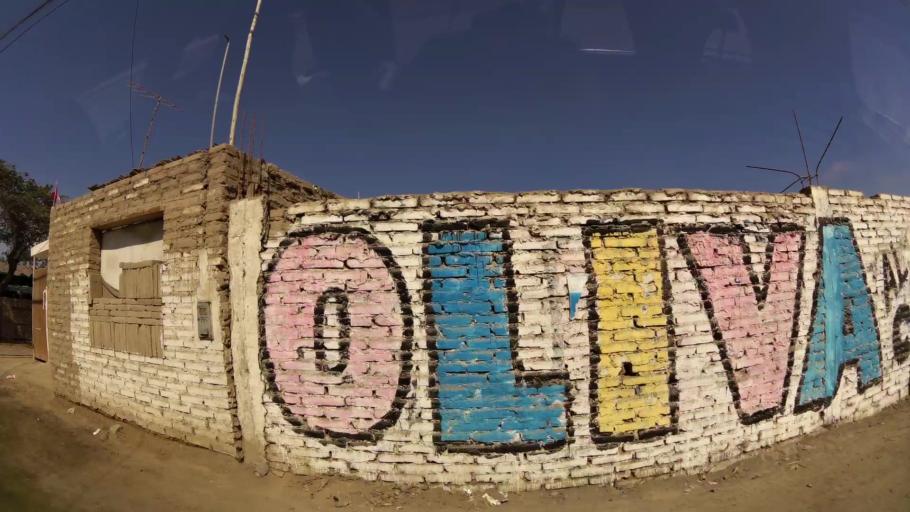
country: PE
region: Ica
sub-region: Provincia de Chincha
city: Sunampe
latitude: -13.4183
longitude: -76.1601
